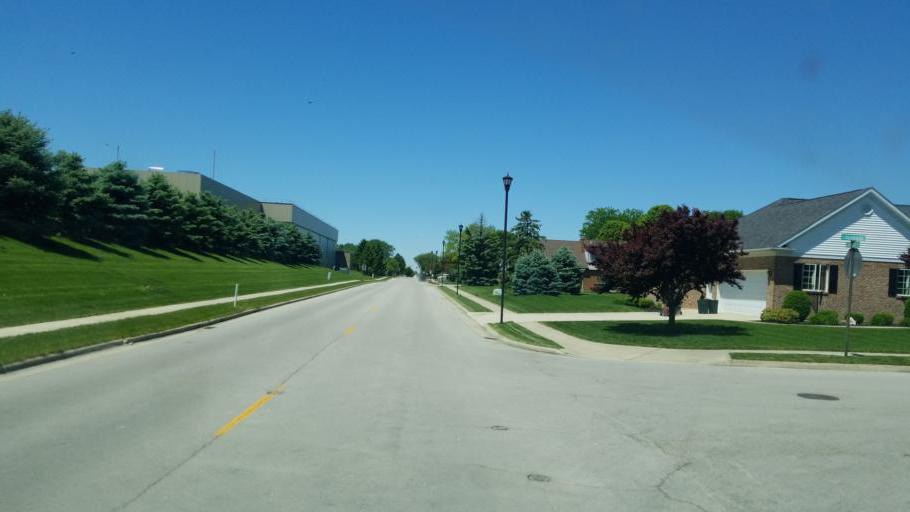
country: US
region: Ohio
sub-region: Auglaize County
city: Minster
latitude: 40.3858
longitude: -84.3722
